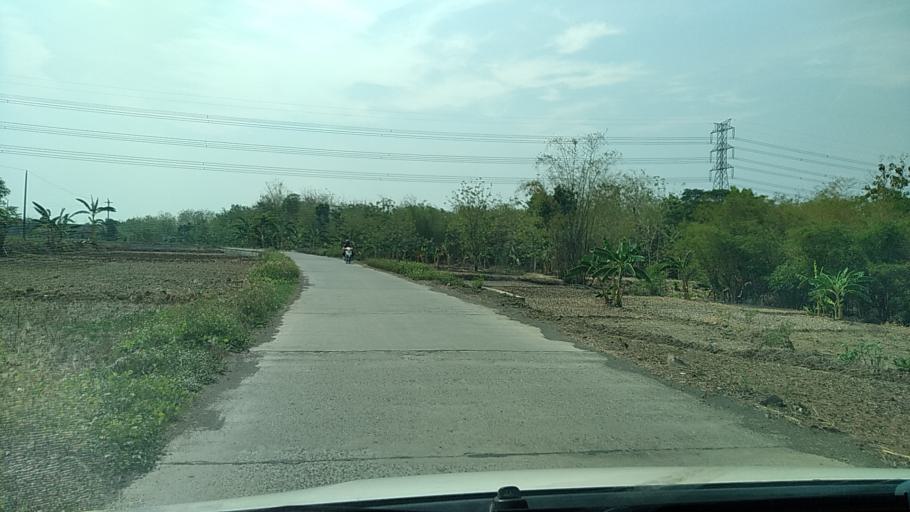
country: ID
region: Central Java
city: Mranggen
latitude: -7.0665
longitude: 110.4919
